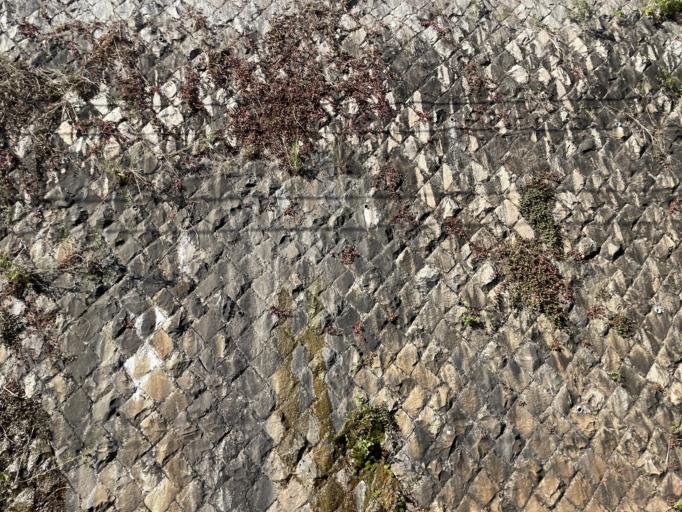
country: JP
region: Nara
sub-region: Ikoma-shi
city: Ikoma
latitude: 34.6913
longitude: 135.7232
